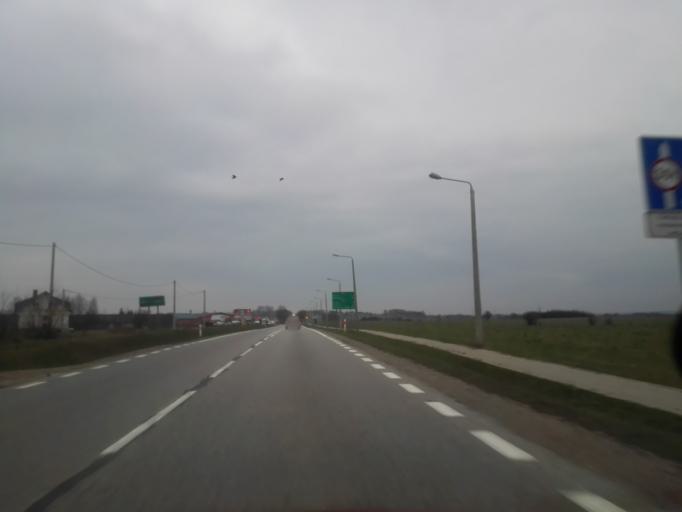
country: PL
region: Podlasie
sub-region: Powiat lomzynski
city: Piatnica
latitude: 53.2461
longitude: 22.1186
